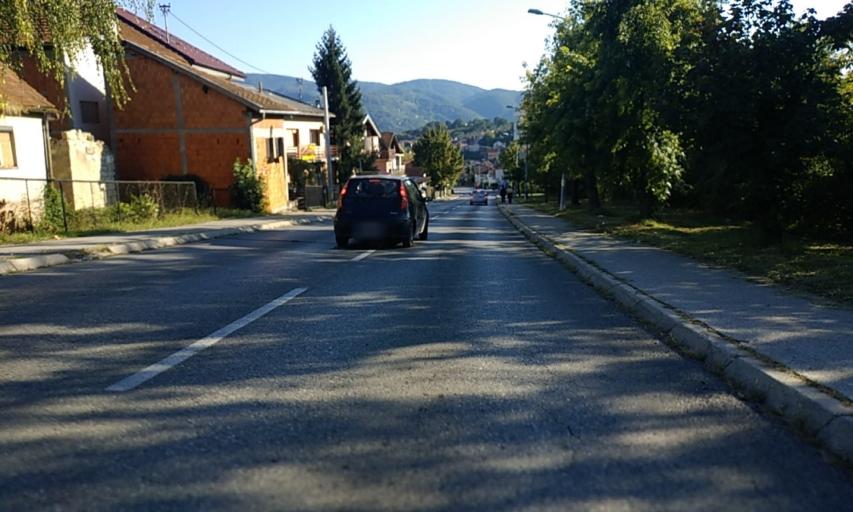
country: BA
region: Republika Srpska
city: Banja Luka
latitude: 44.7781
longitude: 17.1783
